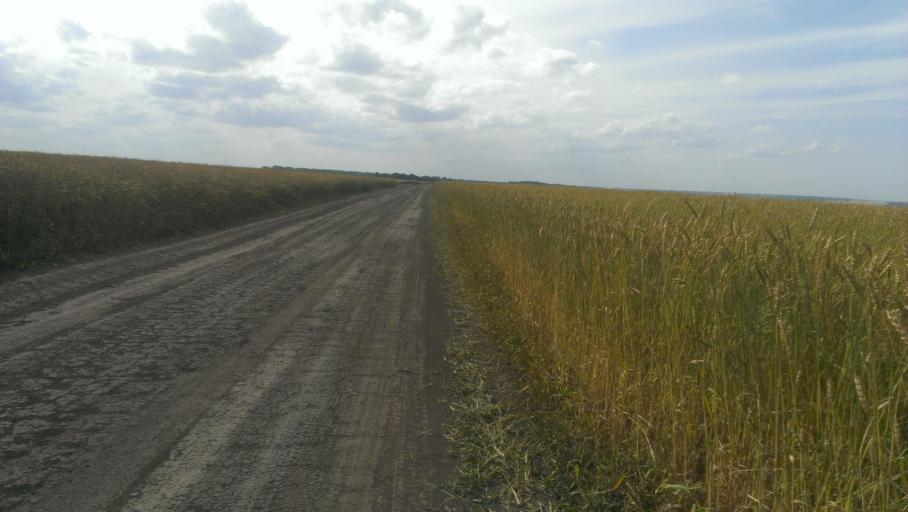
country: RU
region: Altai Krai
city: Gon'ba
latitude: 53.3747
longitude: 83.5527
